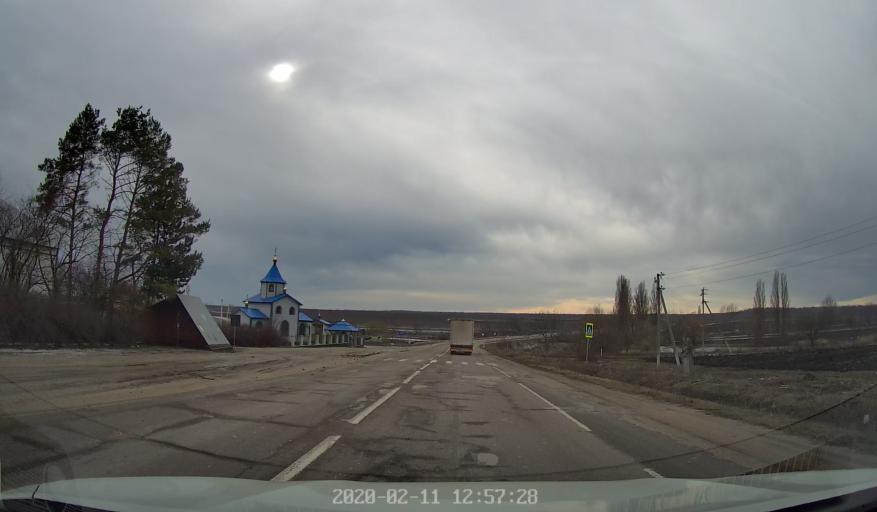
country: MD
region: Briceni
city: Briceni
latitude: 48.3405
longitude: 27.0667
